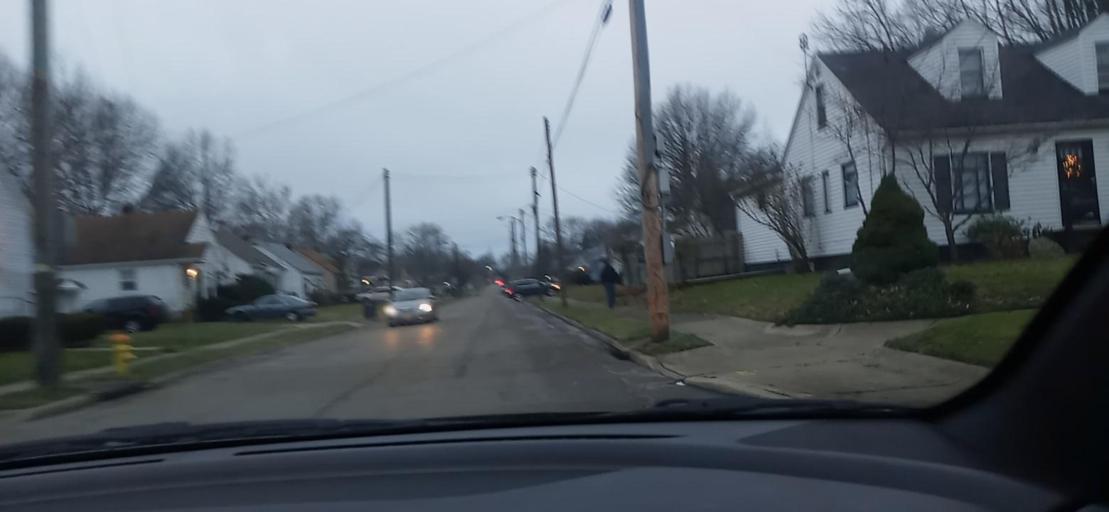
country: US
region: Ohio
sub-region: Summit County
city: Akron
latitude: 41.0445
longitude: -81.5030
